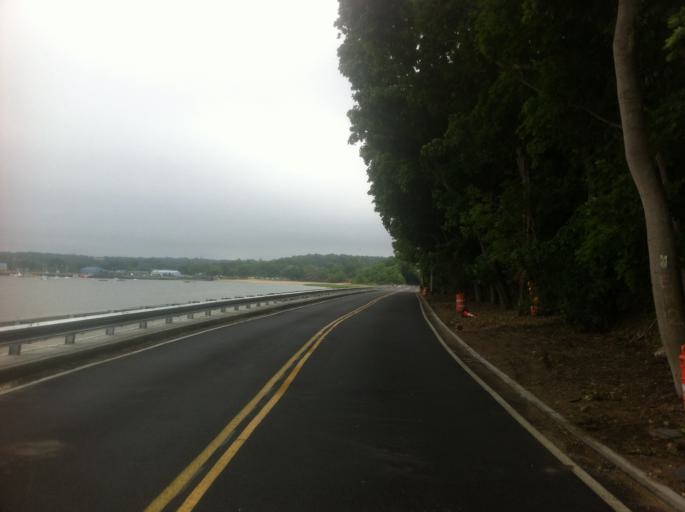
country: US
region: New York
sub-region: Nassau County
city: Oyster Bay
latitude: 40.8808
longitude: -73.5498
